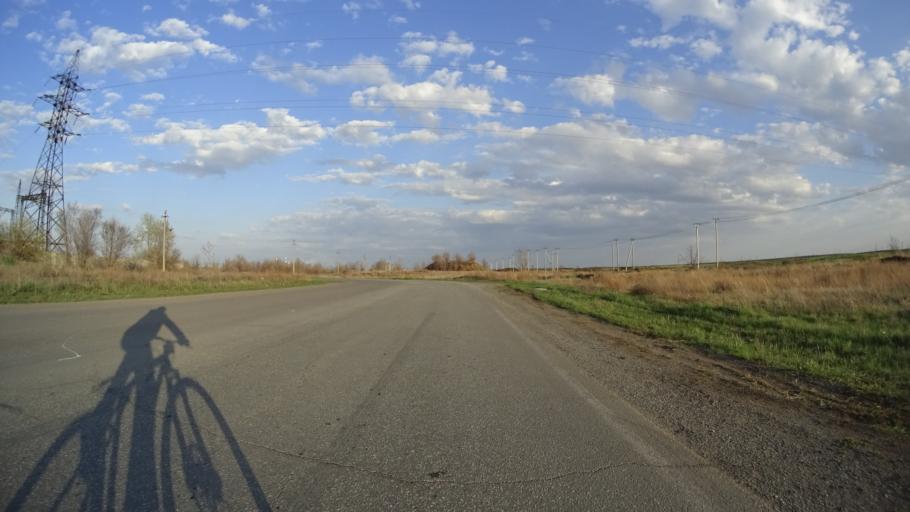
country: RU
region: Chelyabinsk
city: Troitsk
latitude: 54.0626
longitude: 61.5716
